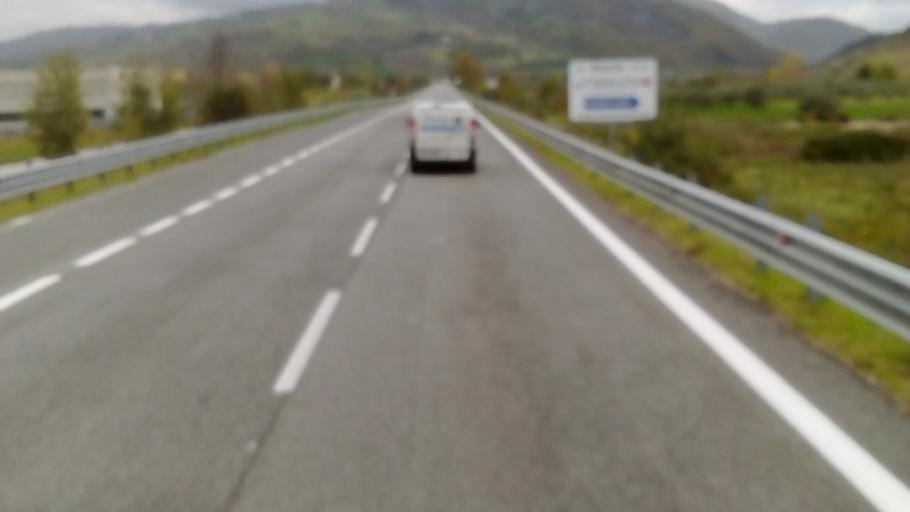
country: IT
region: Abruzzo
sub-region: Provincia di Chieti
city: San Giovanni Lipioni
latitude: 41.8080
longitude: 14.5671
